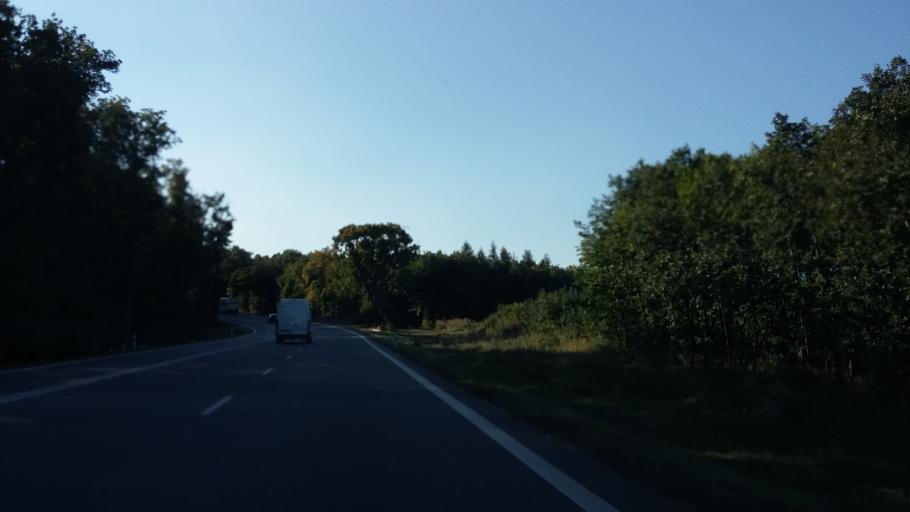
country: CZ
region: South Moravian
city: Troubsko
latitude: 49.1879
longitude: 16.4698
